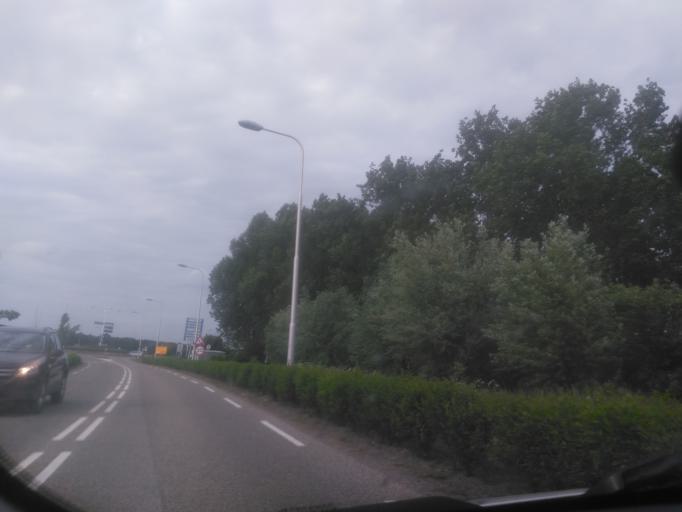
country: NL
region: Zeeland
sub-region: Gemeente Hulst
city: Hulst
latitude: 51.2766
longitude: 4.0630
